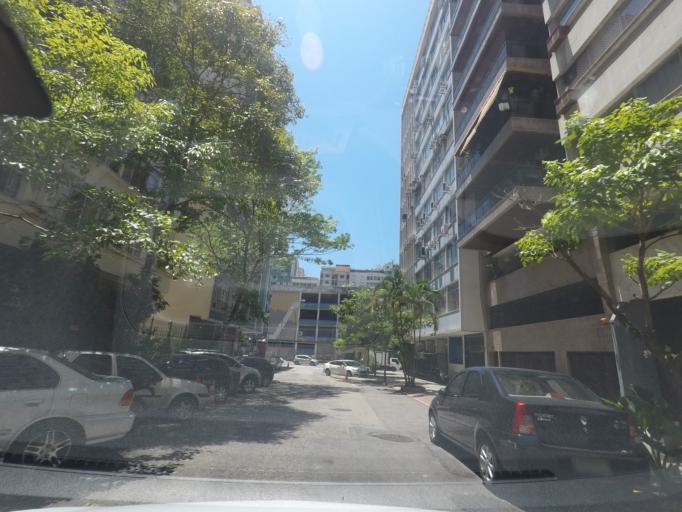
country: BR
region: Rio de Janeiro
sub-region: Rio De Janeiro
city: Rio de Janeiro
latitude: -22.9642
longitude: -43.1814
